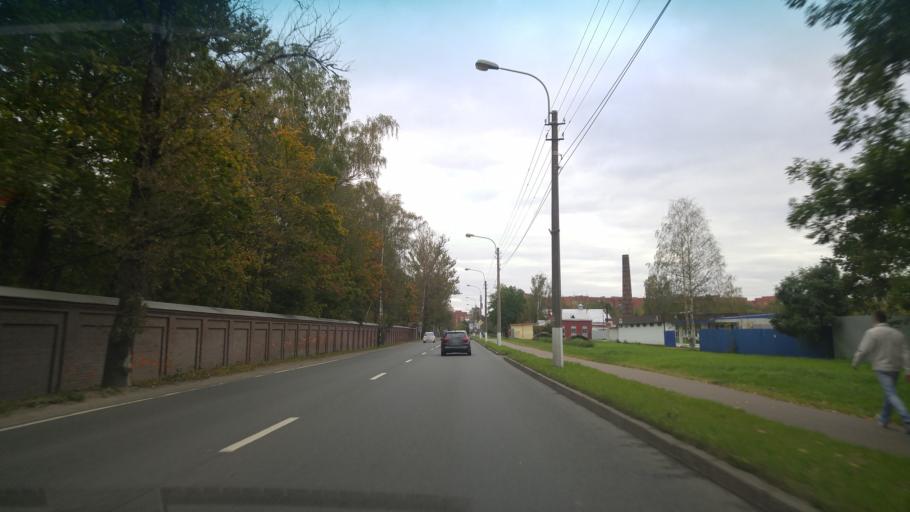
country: RU
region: St.-Petersburg
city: Kronshtadt
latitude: 60.0047
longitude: 29.7504
